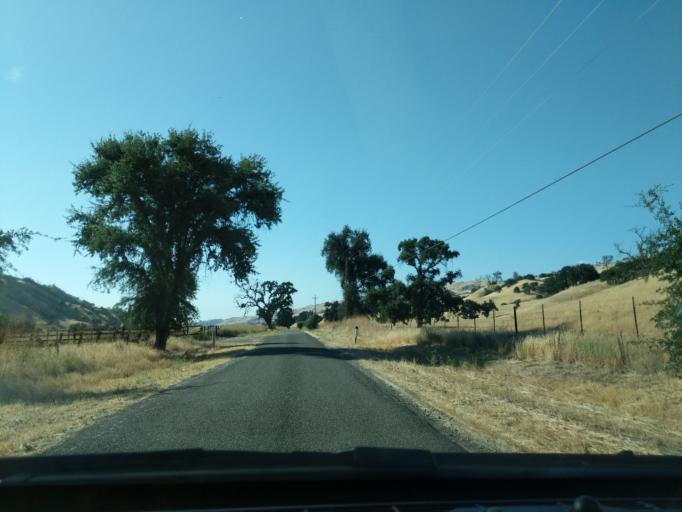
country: US
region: California
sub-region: San Luis Obispo County
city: San Miguel
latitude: 36.1346
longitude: -120.7472
